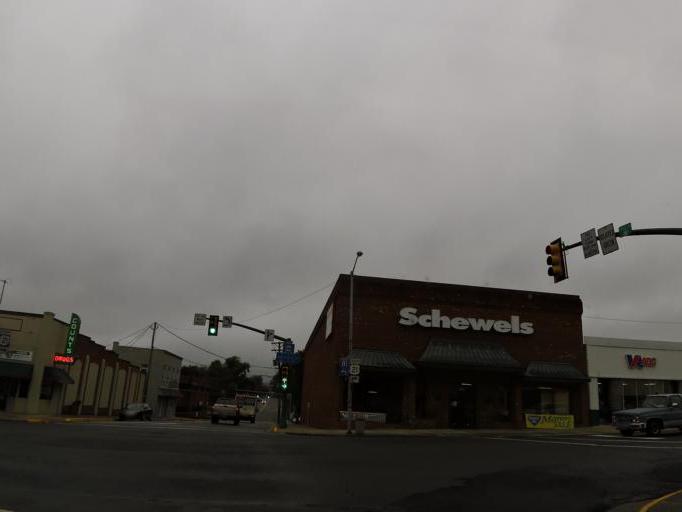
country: US
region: Virginia
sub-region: Wythe County
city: Wytheville
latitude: 36.9486
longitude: -81.0853
